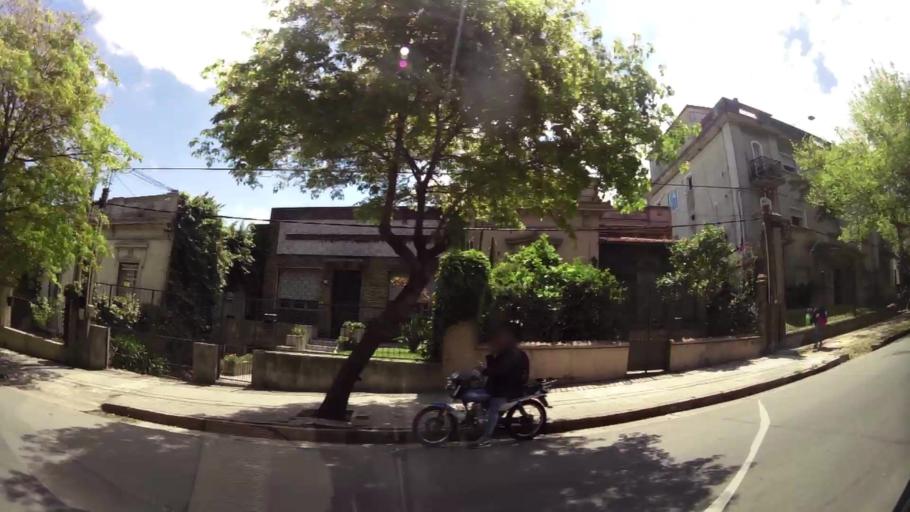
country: UY
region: Montevideo
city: Montevideo
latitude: -34.8559
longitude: -56.2118
